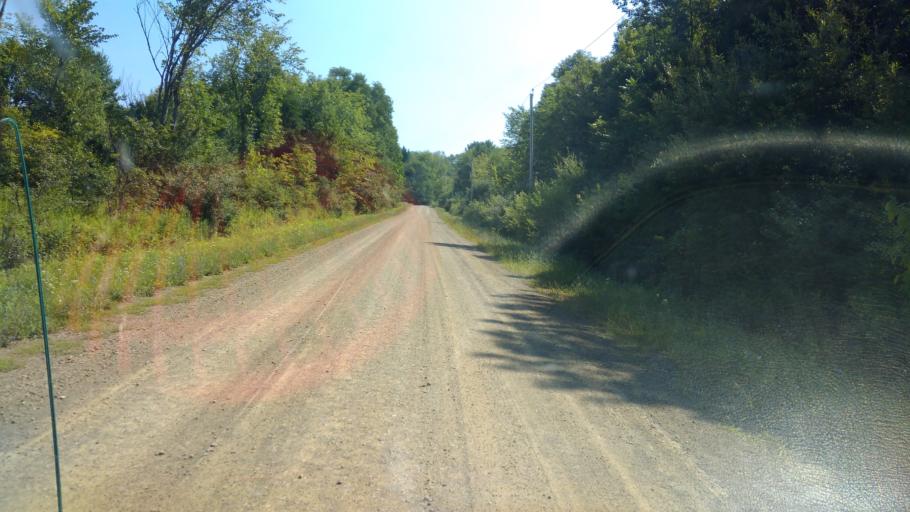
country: US
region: New York
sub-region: Allegany County
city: Houghton
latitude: 42.3640
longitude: -78.0442
